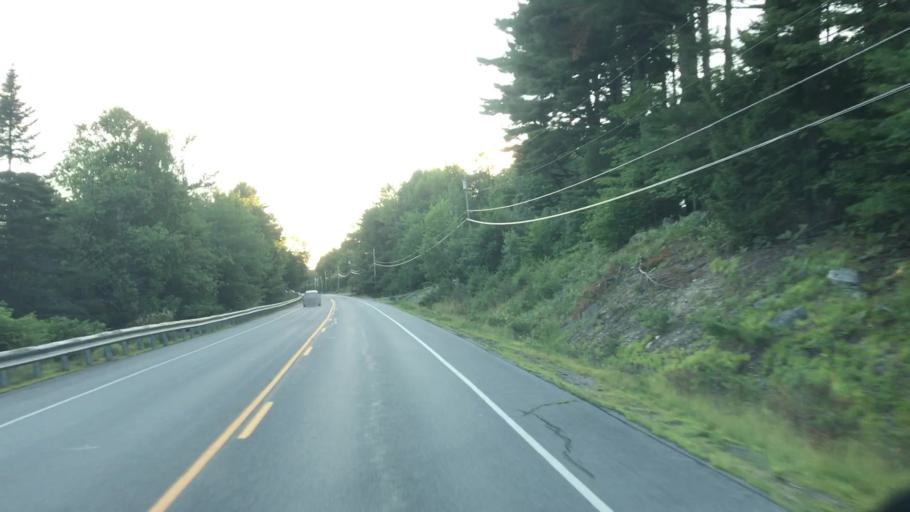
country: US
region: Maine
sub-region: Penobscot County
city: Lincoln
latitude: 45.3743
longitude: -68.4767
